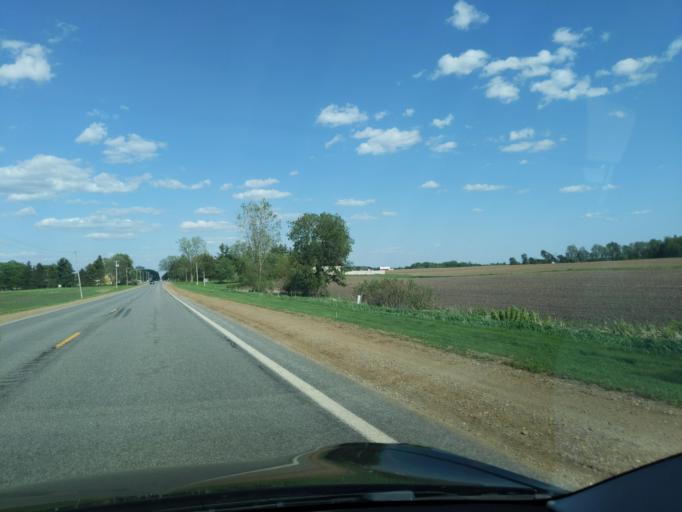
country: US
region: Michigan
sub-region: Ionia County
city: Lake Odessa
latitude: 42.7560
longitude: -85.0120
